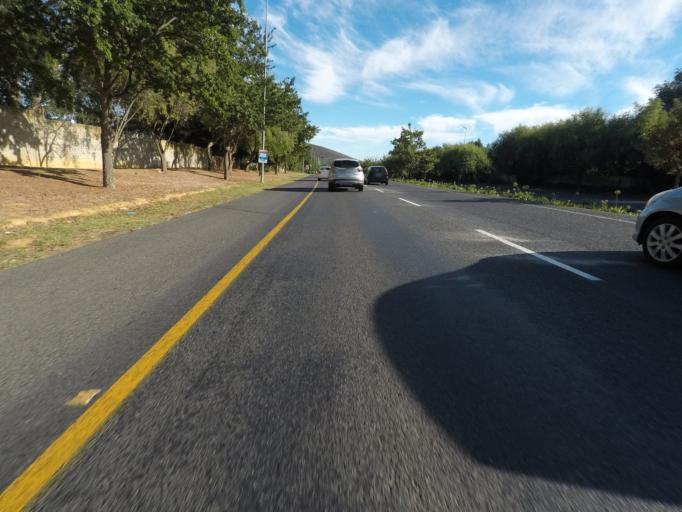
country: ZA
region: Western Cape
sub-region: Cape Winelands District Municipality
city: Stellenbosch
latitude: -33.9519
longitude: 18.8554
